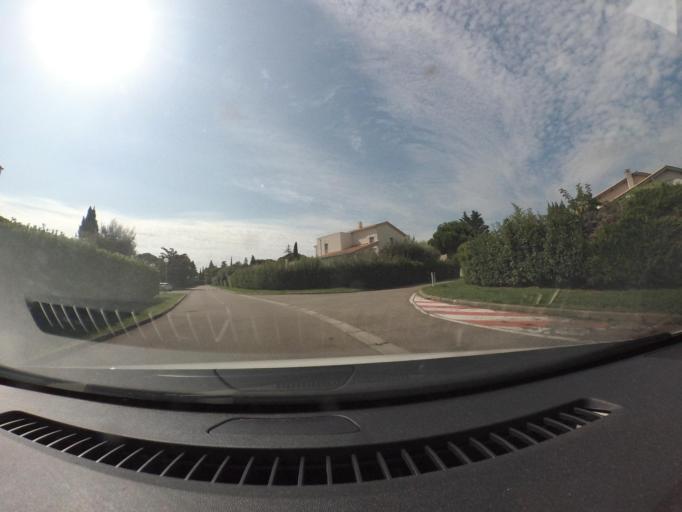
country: FR
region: Languedoc-Roussillon
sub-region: Departement de l'Herault
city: Baillargues
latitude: 43.6505
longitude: 4.0076
